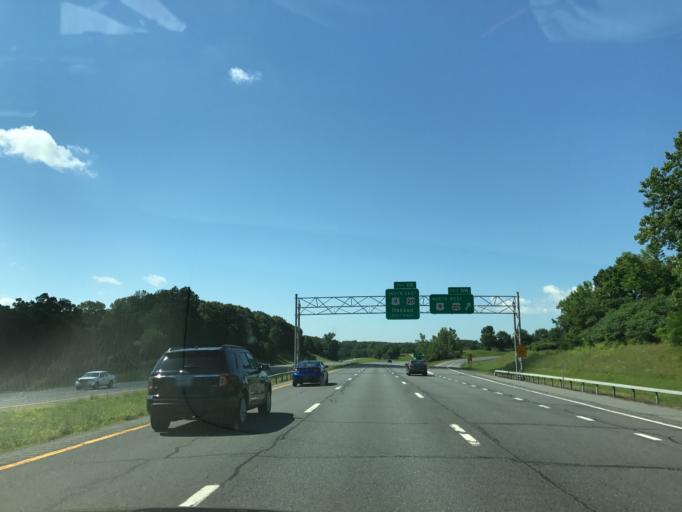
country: US
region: New York
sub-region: Rensselaer County
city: East Greenbush
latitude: 42.5642
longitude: -73.6789
